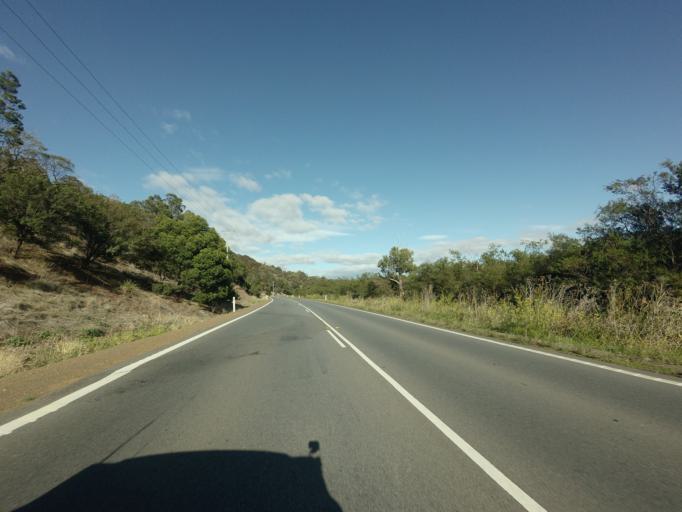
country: AU
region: Tasmania
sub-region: Derwent Valley
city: New Norfolk
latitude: -42.7717
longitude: 147.1386
